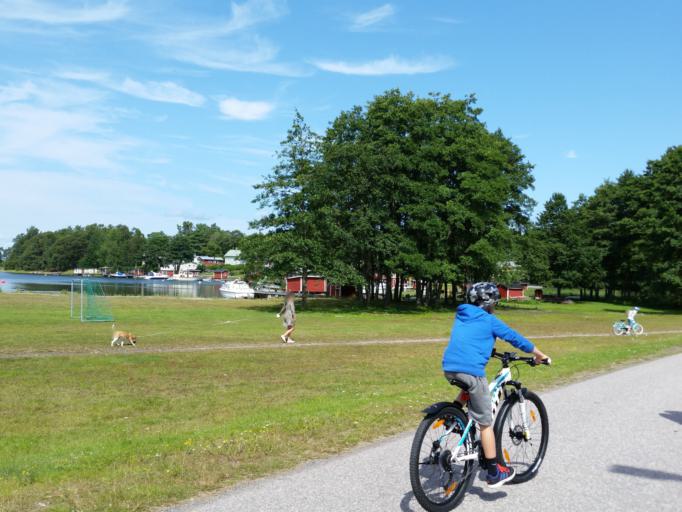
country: FI
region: Uusimaa
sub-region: Raaseporin
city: Hanko
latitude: 59.8339
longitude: 22.9312
